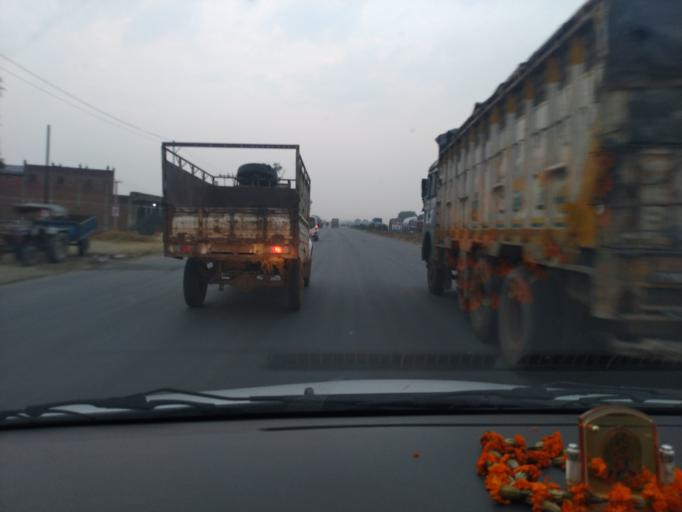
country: IN
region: Bihar
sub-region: Kaimur District
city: Bhabua
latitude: 25.2177
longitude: 83.5044
